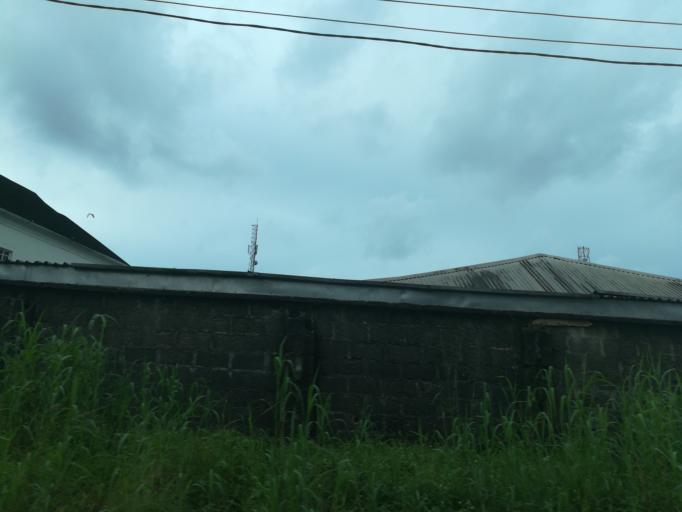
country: NG
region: Rivers
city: Port Harcourt
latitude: 4.8129
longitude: 6.9880
